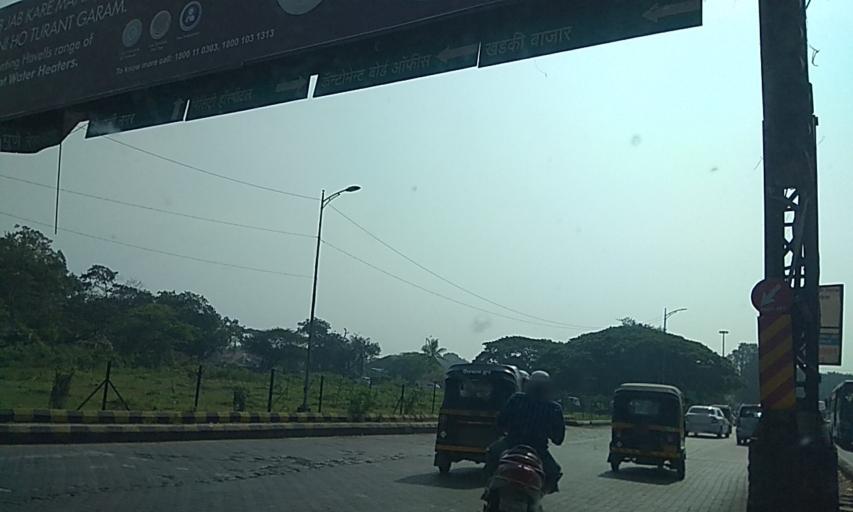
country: IN
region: Maharashtra
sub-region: Pune Division
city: Khadki
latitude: 18.5572
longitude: 73.8465
